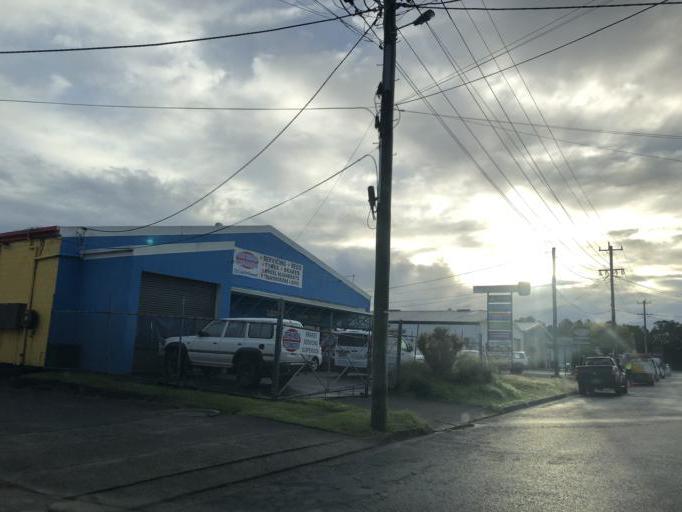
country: AU
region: New South Wales
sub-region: Coffs Harbour
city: Coffs Harbour
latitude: -30.2895
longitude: 153.1288
